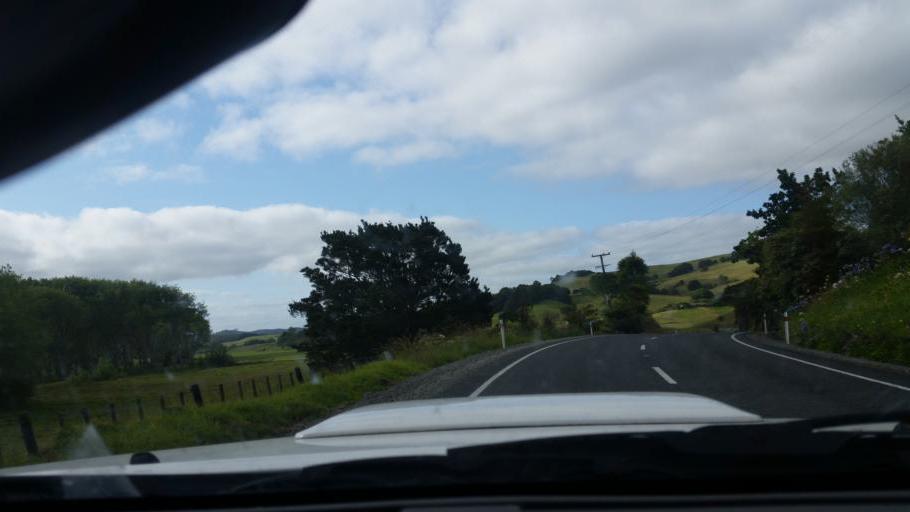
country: NZ
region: Northland
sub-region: Kaipara District
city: Dargaville
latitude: -35.8449
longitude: 173.8442
